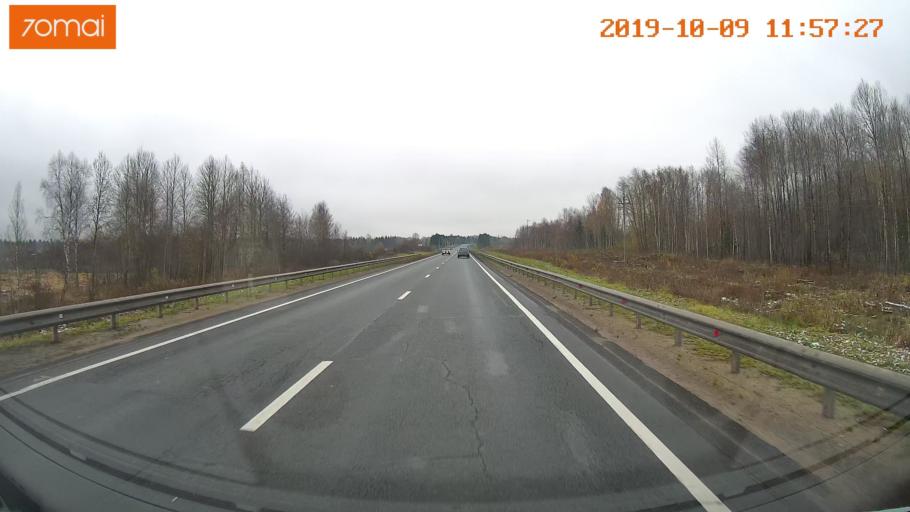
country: RU
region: Vologda
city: Gryazovets
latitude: 58.7321
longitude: 40.2927
